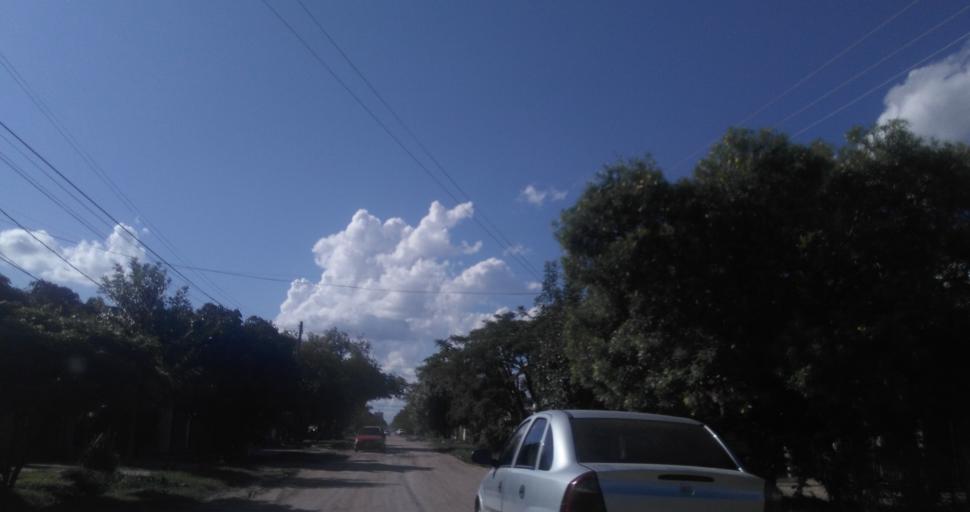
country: AR
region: Chaco
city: Resistencia
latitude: -27.4755
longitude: -58.9660
